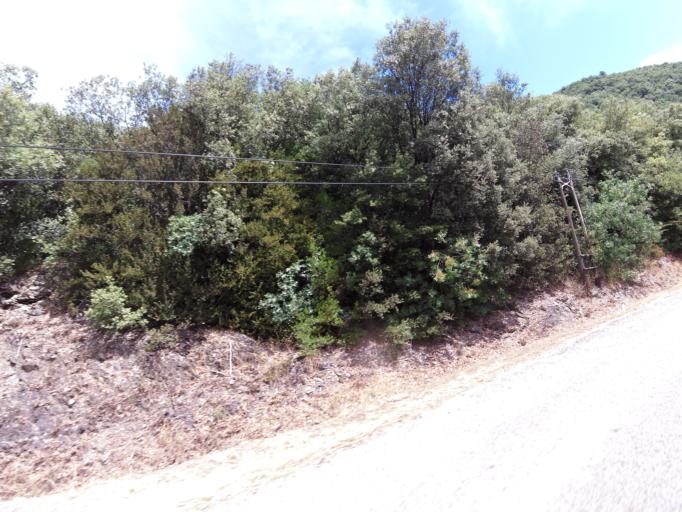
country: FR
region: Languedoc-Roussillon
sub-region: Departement du Gard
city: Sumene
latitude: 43.9934
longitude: 3.6875
